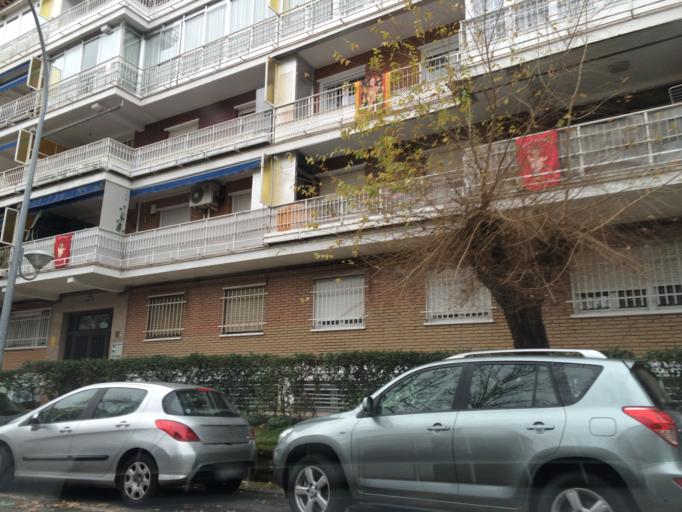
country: ES
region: Madrid
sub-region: Provincia de Madrid
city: Alcorcon
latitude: 40.3517
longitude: -3.8212
